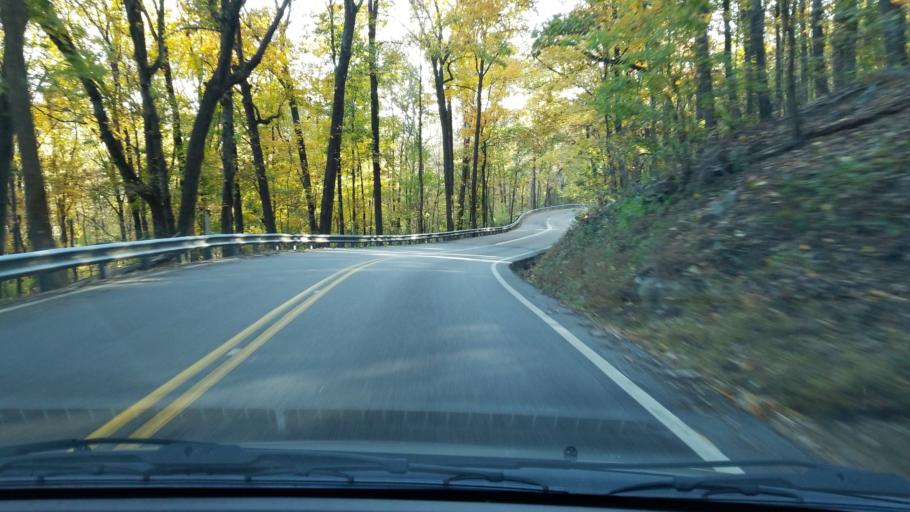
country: US
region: Tennessee
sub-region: Hamilton County
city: Falling Water
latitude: 35.2096
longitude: -85.2608
